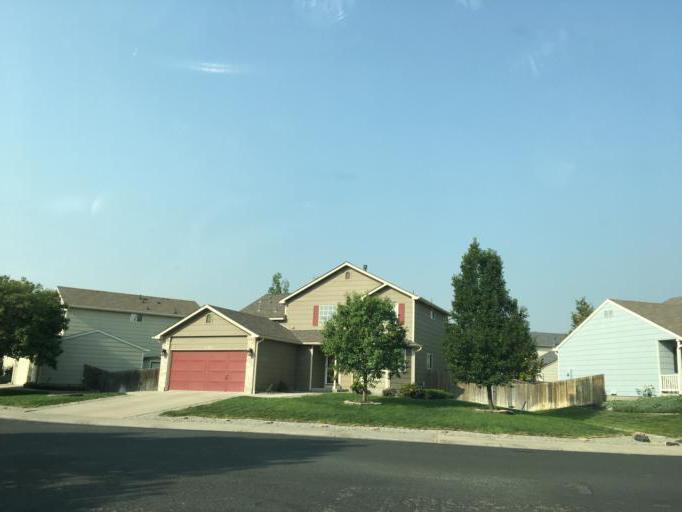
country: US
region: Colorado
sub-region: Adams County
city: Todd Creek
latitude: 39.9083
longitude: -104.8525
